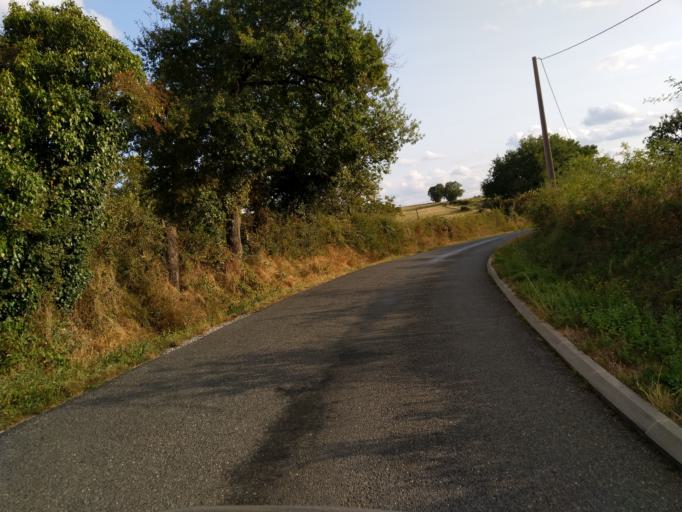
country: FR
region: Midi-Pyrenees
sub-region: Departement du Tarn
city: Frejairolles
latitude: 43.8738
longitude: 2.2345
